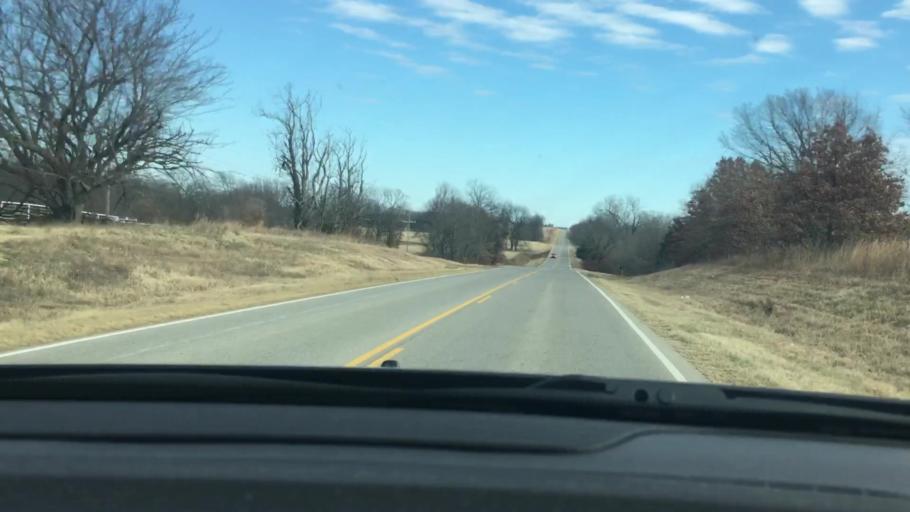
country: US
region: Oklahoma
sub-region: Garvin County
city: Stratford
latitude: 34.7969
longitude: -96.8434
